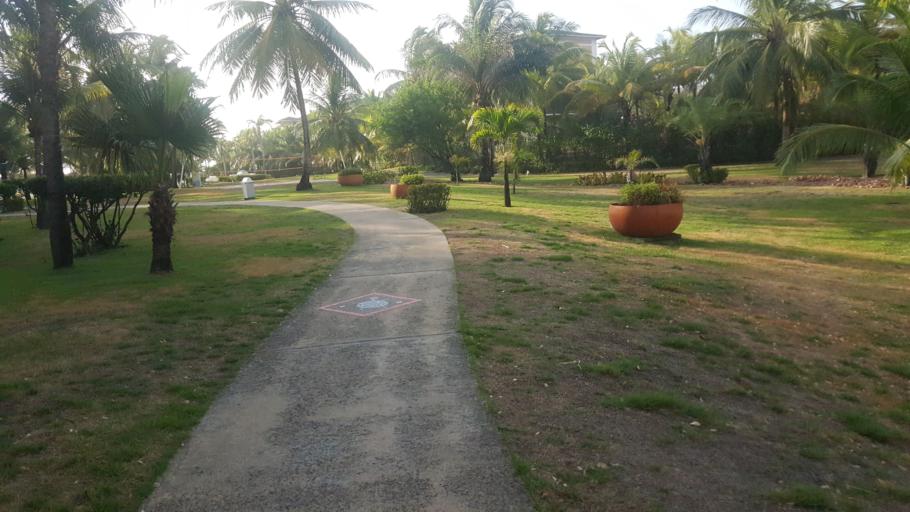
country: BR
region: Bahia
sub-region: Mata De Sao Joao
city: Mata de Sao Joao
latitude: -12.4384
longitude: -37.9185
